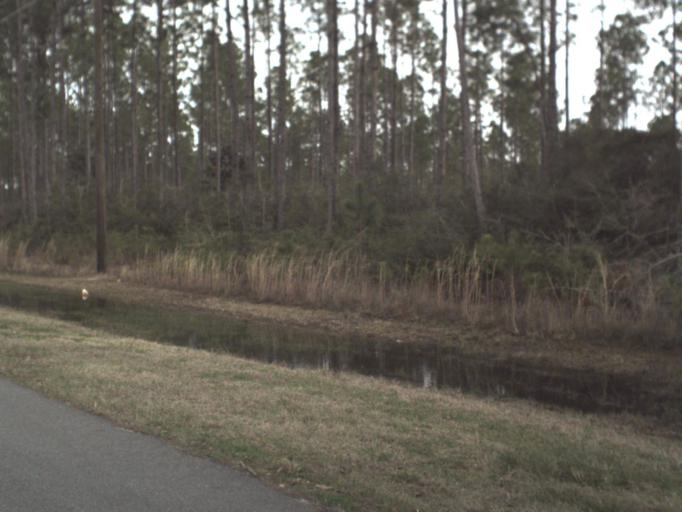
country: US
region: Florida
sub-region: Bay County
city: Callaway
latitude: 30.1518
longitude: -85.4850
